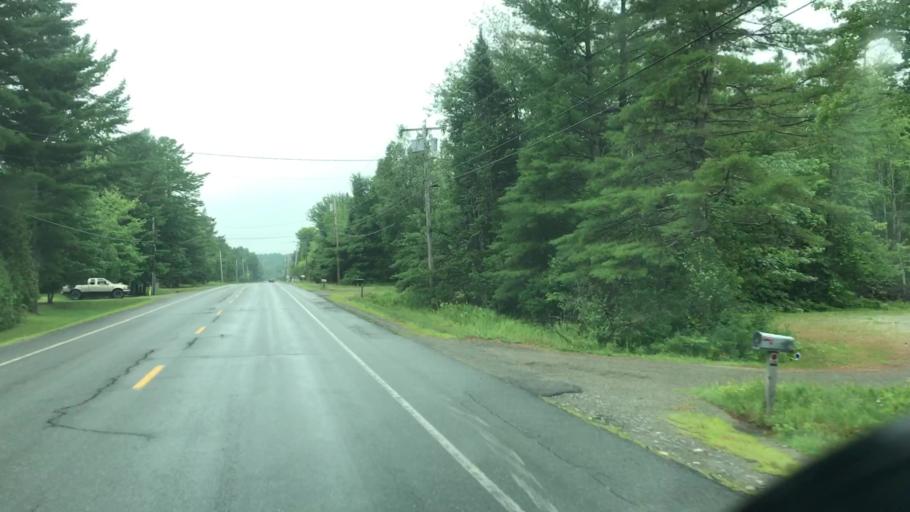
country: US
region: Maine
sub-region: Penobscot County
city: Lincoln
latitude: 45.3448
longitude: -68.5578
